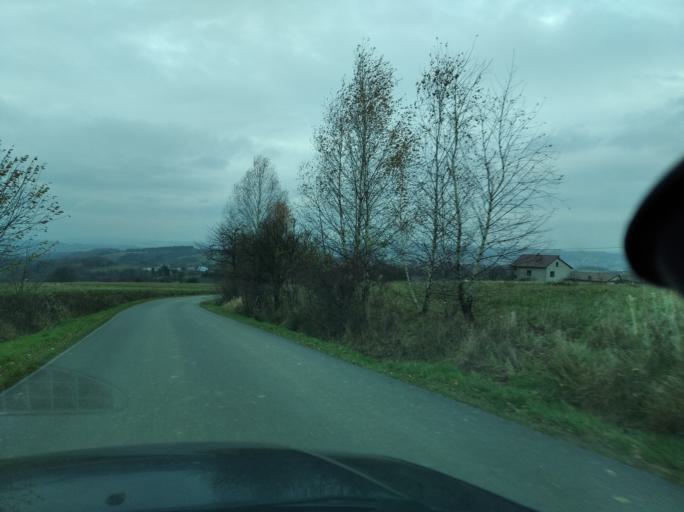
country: PL
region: Subcarpathian Voivodeship
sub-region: Powiat strzyzowski
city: Wysoka Strzyzowska
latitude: 49.8361
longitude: 21.7757
